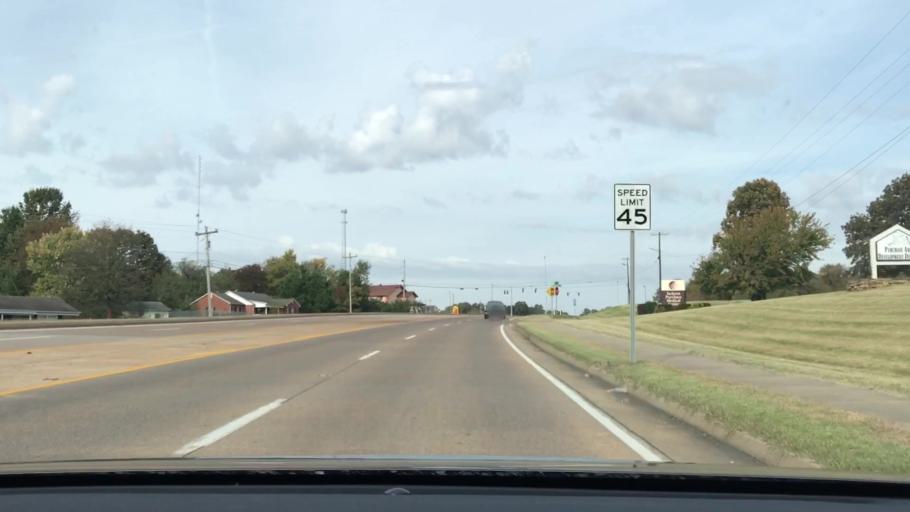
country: US
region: Kentucky
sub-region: Graves County
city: Mayfield
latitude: 36.7534
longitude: -88.6527
